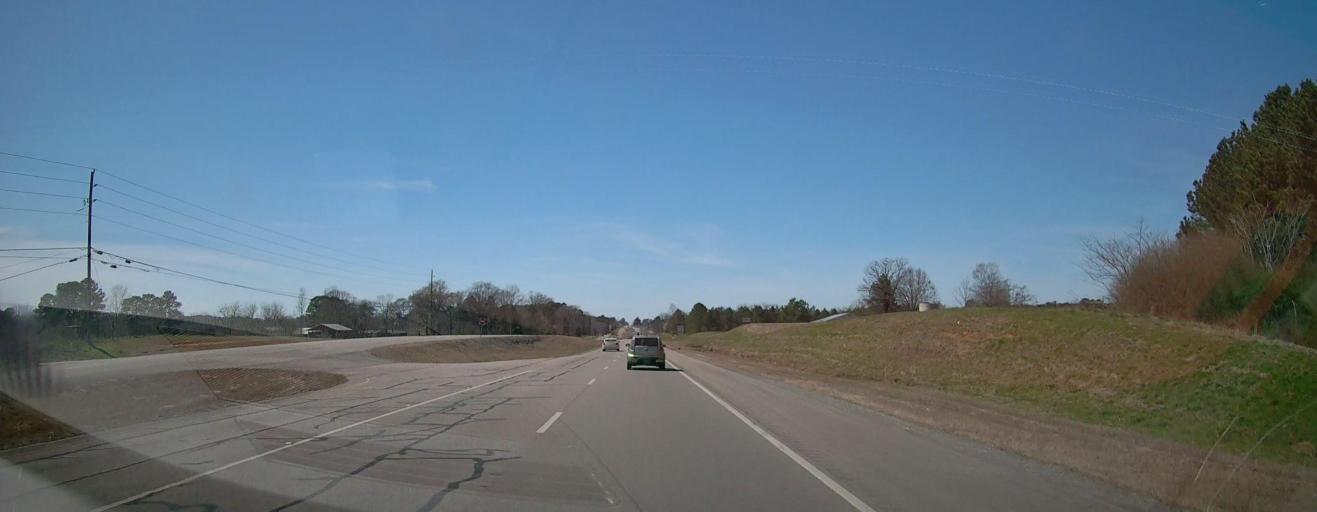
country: US
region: Alabama
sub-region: Cullman County
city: Hanceville
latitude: 34.1754
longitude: -86.7159
